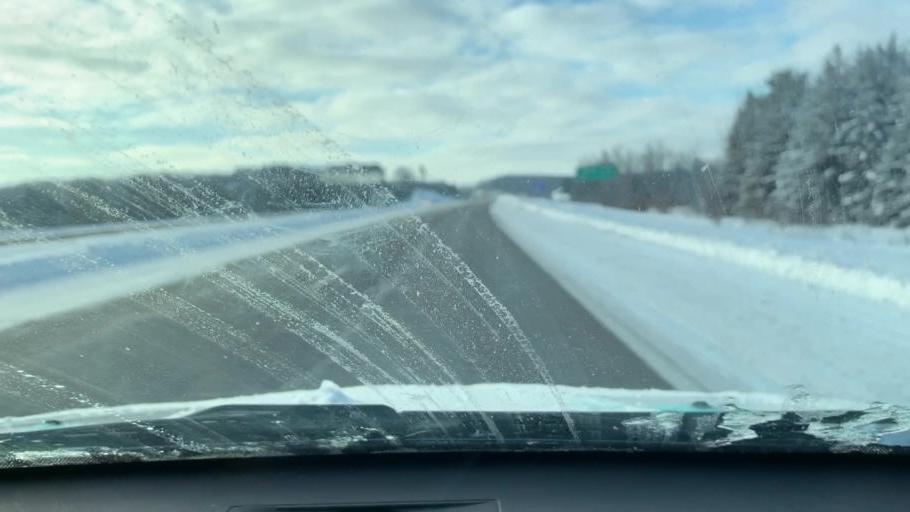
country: US
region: Michigan
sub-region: Wexford County
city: Cadillac
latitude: 44.3087
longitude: -85.3925
